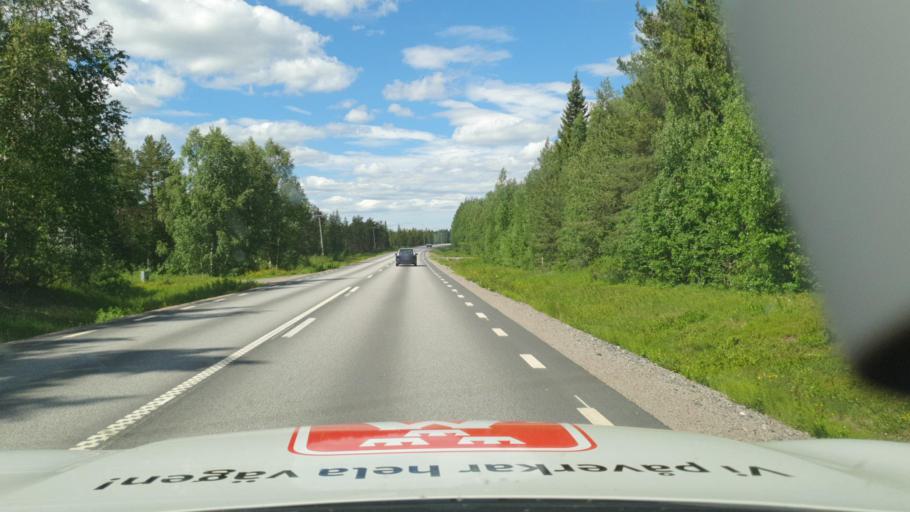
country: SE
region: Vaesterbotten
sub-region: Skelleftea Kommun
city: Langsele
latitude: 65.0236
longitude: 20.1221
